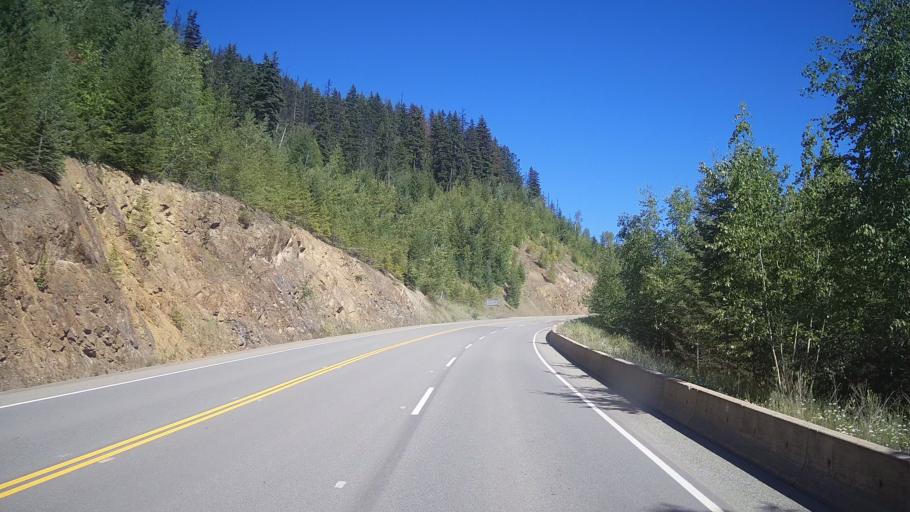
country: CA
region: British Columbia
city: Kamloops
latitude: 51.4884
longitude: -120.2676
